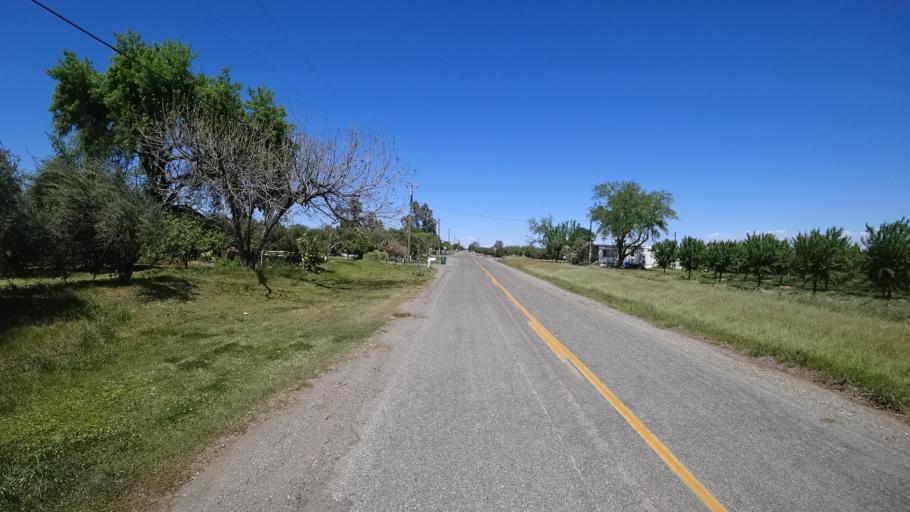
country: US
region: California
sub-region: Glenn County
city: Orland
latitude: 39.7862
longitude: -122.1784
